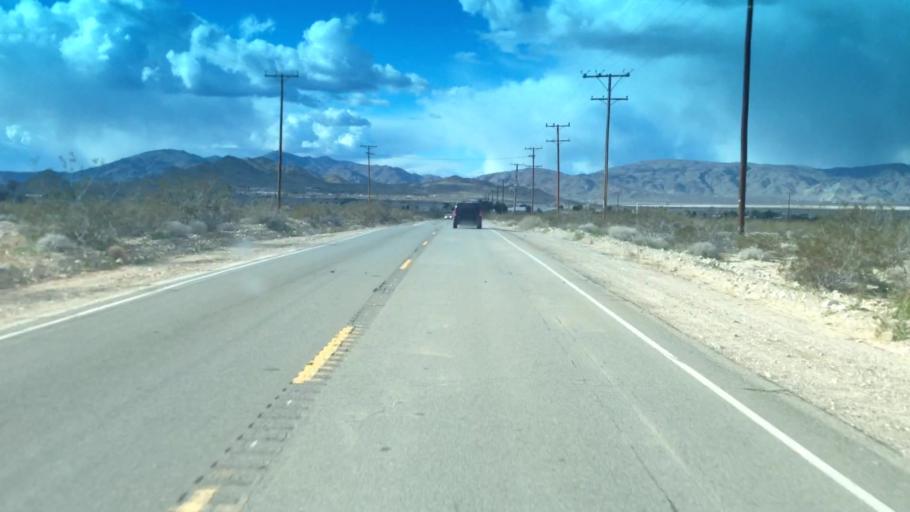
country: US
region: California
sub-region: San Bernardino County
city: Lucerne Valley
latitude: 34.4339
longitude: -116.9373
